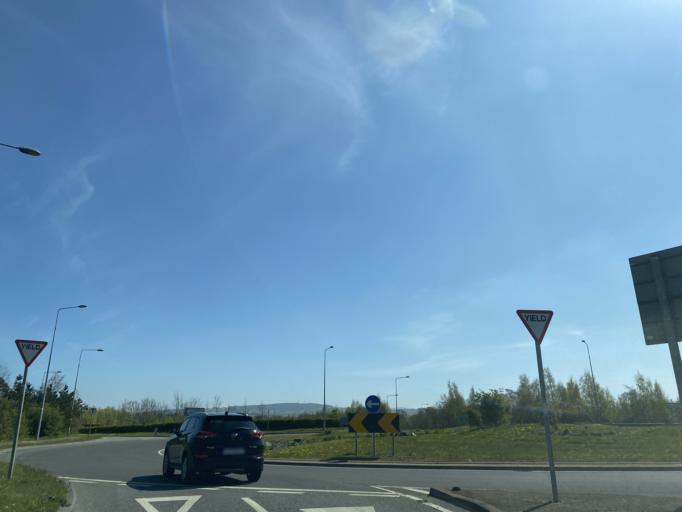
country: IE
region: Leinster
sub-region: Kildare
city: Kill
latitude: 53.2535
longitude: -6.5768
